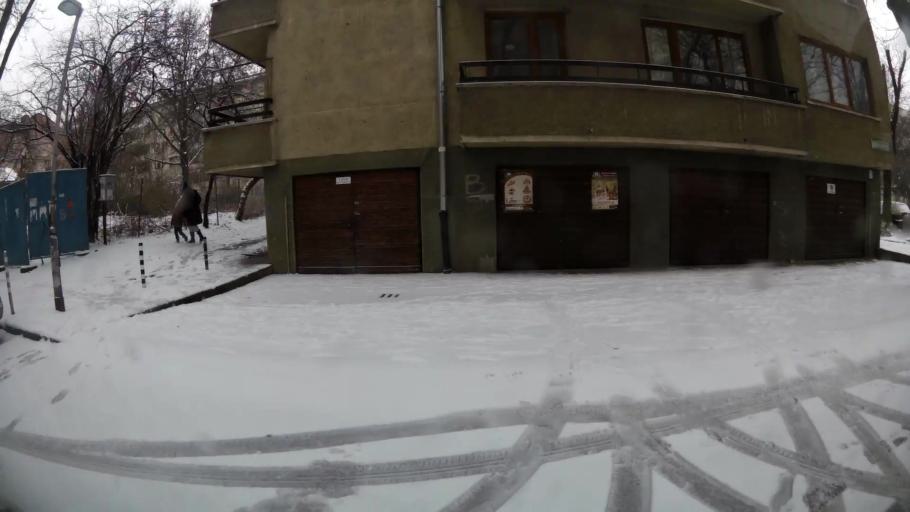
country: BG
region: Sofia-Capital
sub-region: Stolichna Obshtina
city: Sofia
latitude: 42.6872
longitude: 23.3062
